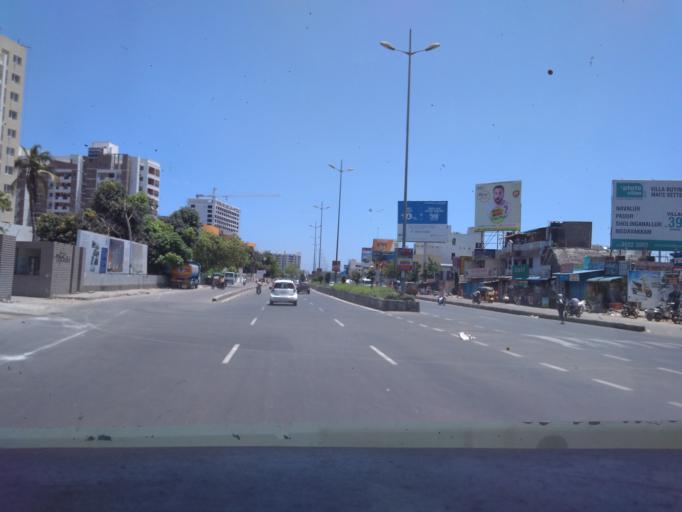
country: IN
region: Tamil Nadu
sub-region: Kancheepuram
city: Injambakkam
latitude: 12.8392
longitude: 80.2279
